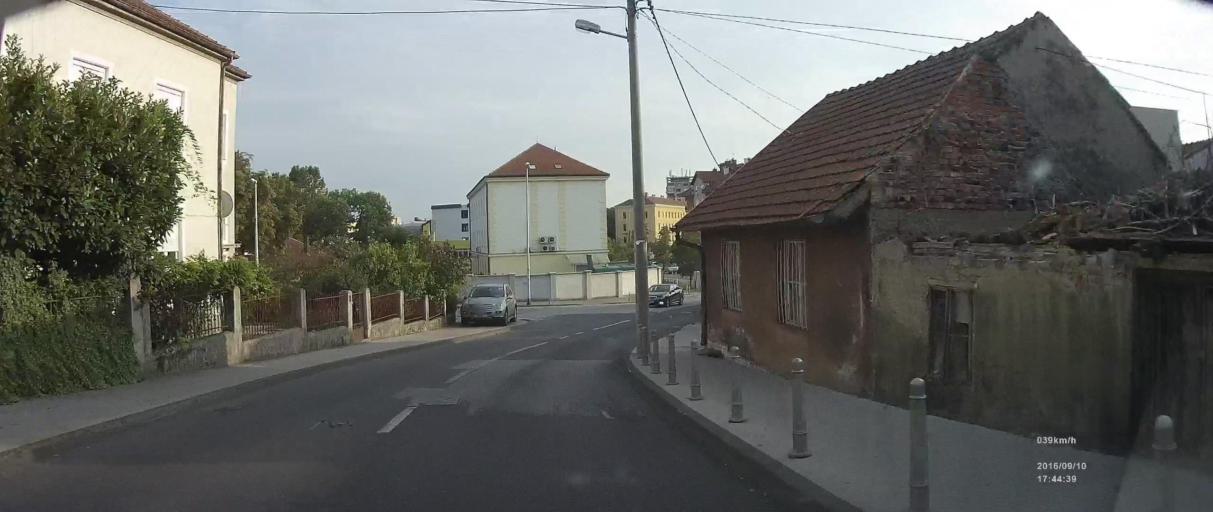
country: HR
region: Grad Zagreb
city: Zagreb - Centar
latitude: 45.8181
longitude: 15.9375
